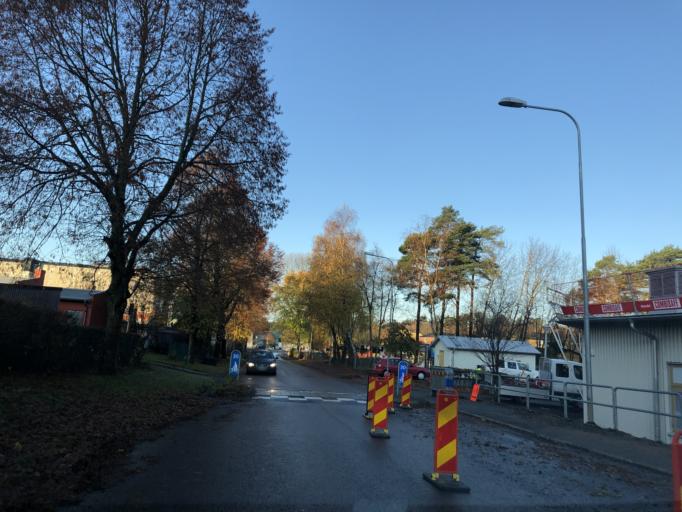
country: SE
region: Vaestra Goetaland
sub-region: Goteborg
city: Hammarkullen
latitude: 57.7815
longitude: 12.0391
